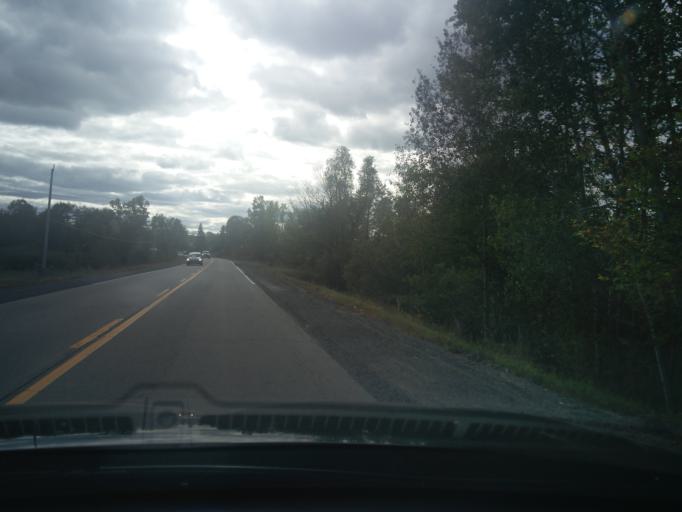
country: CA
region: Ontario
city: Perth
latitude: 44.7345
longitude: -76.3950
